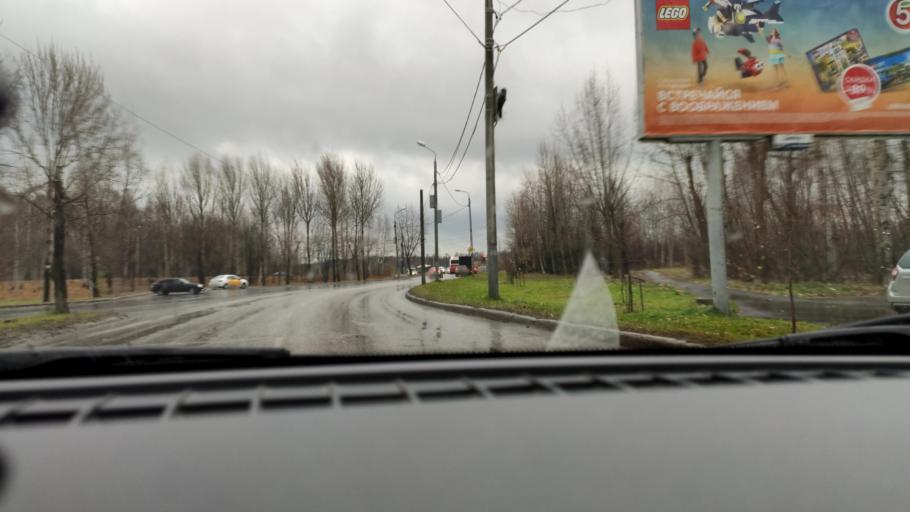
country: RU
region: Perm
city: Perm
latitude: 58.1025
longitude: 56.3884
